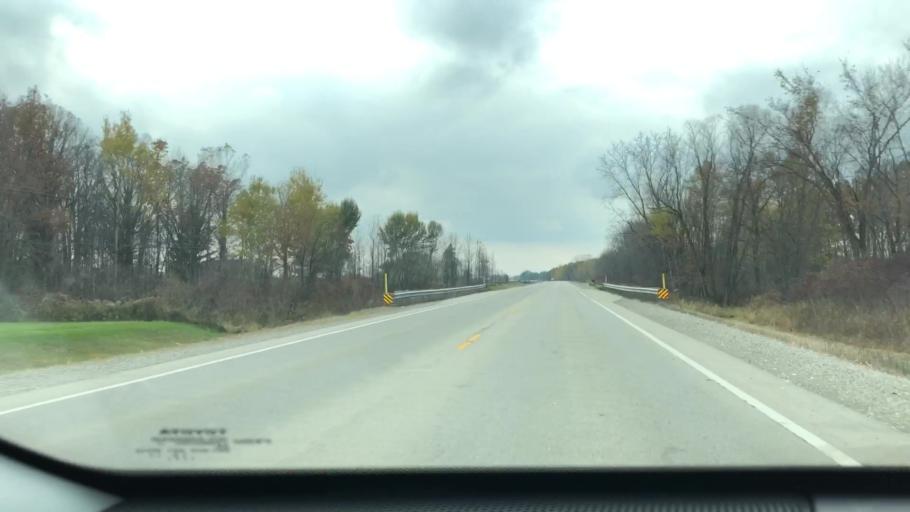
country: US
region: Wisconsin
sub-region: Brown County
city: Oneida
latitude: 44.5023
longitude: -88.2338
